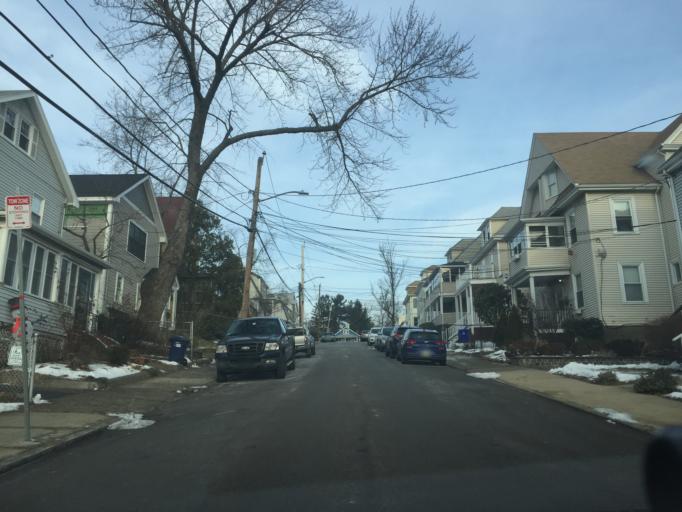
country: US
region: Massachusetts
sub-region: Middlesex County
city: Watertown
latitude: 42.3553
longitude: -71.1587
